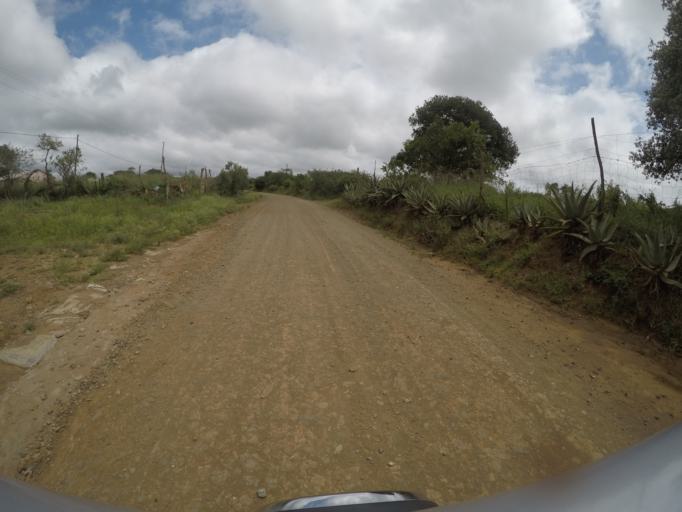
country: ZA
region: KwaZulu-Natal
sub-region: uThungulu District Municipality
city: Empangeni
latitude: -28.5777
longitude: 31.8467
